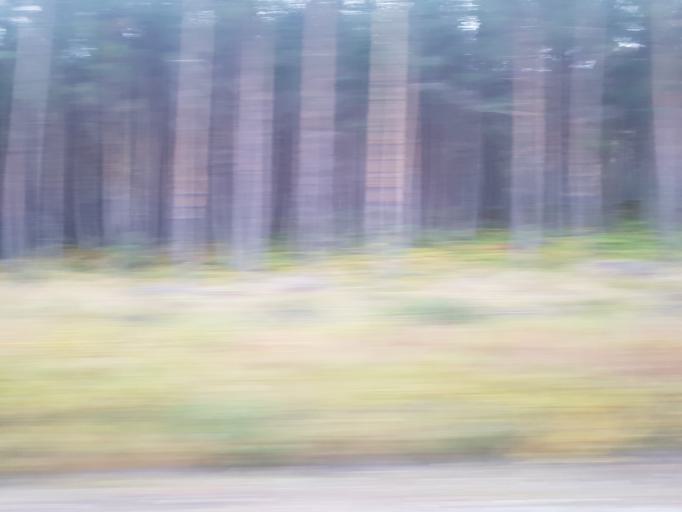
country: NO
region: Oppland
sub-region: Dovre
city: Dovre
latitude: 61.9135
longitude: 9.3536
